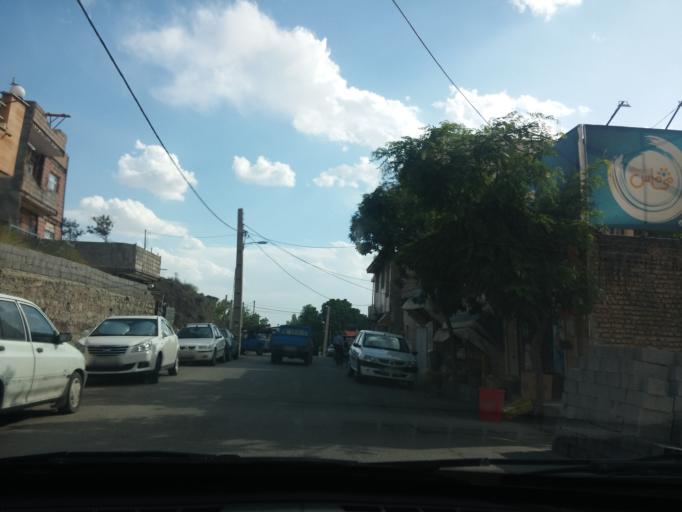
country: IR
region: Tehran
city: Damavand
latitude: 35.7262
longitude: 51.9023
